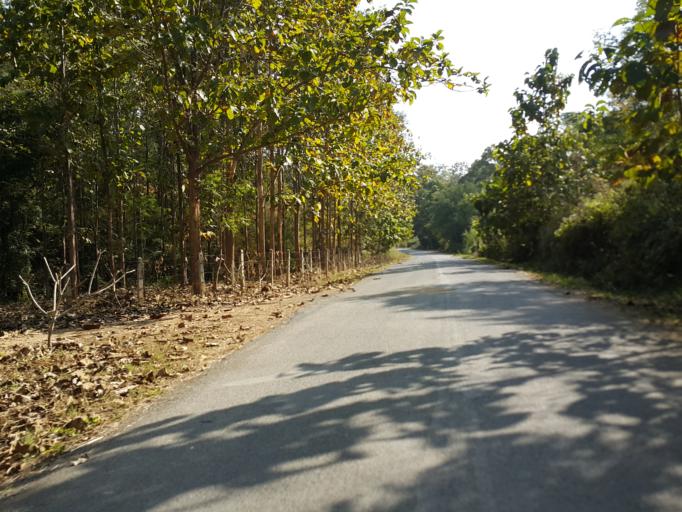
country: TH
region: Chiang Mai
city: Mae On
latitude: 18.7966
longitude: 99.2314
